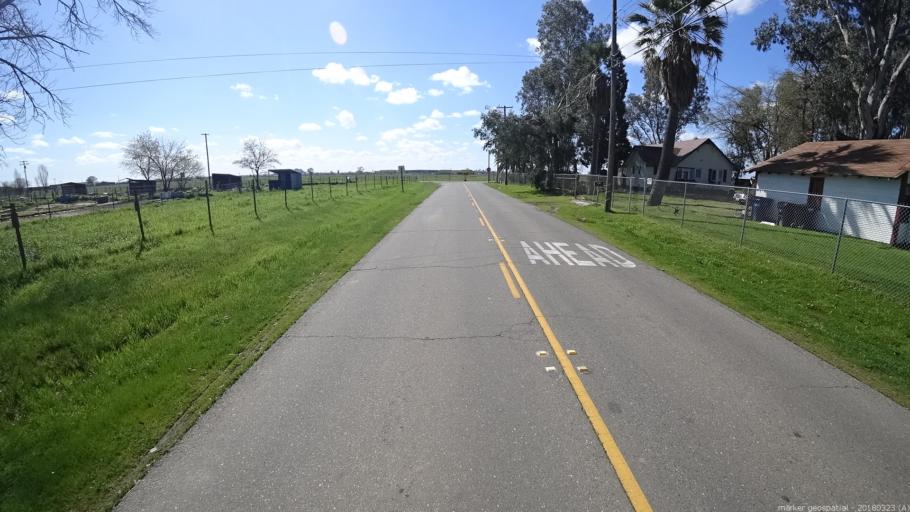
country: US
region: California
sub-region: Sacramento County
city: Rio Linda
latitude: 38.6696
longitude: -121.4199
